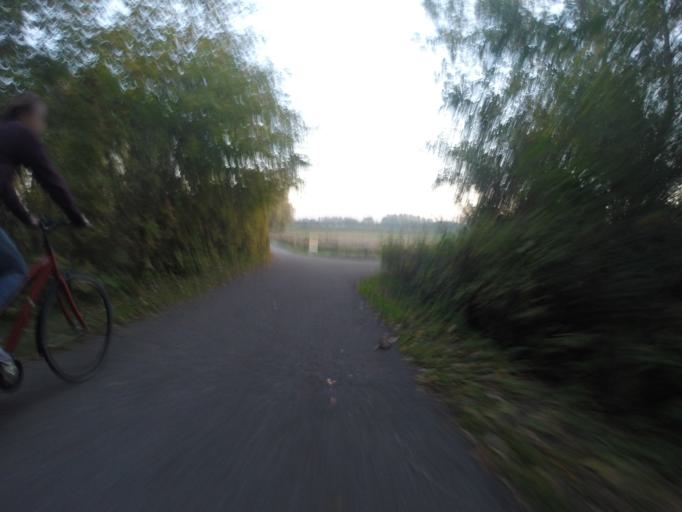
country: DK
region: Capital Region
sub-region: Hoje-Taastrup Kommune
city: Taastrup
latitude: 55.6593
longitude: 12.3232
